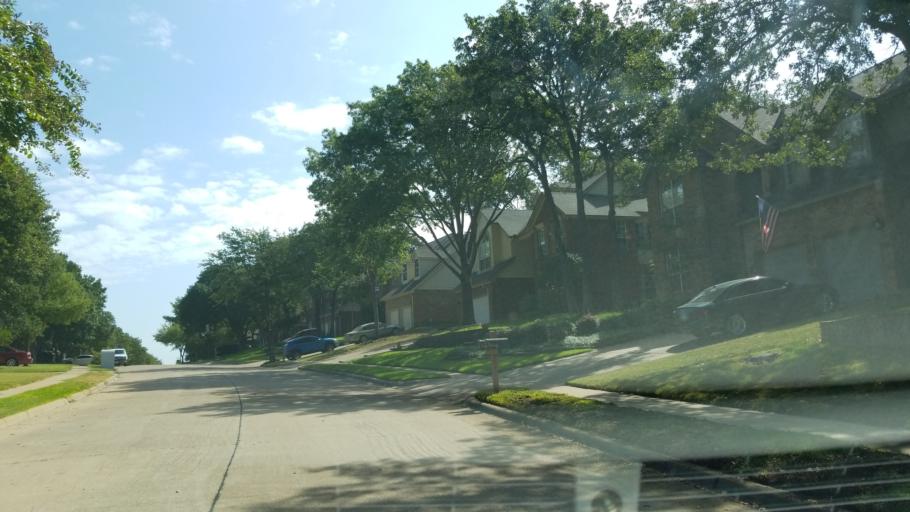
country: US
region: Texas
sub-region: Tarrant County
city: Grapevine
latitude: 32.8873
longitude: -97.0944
